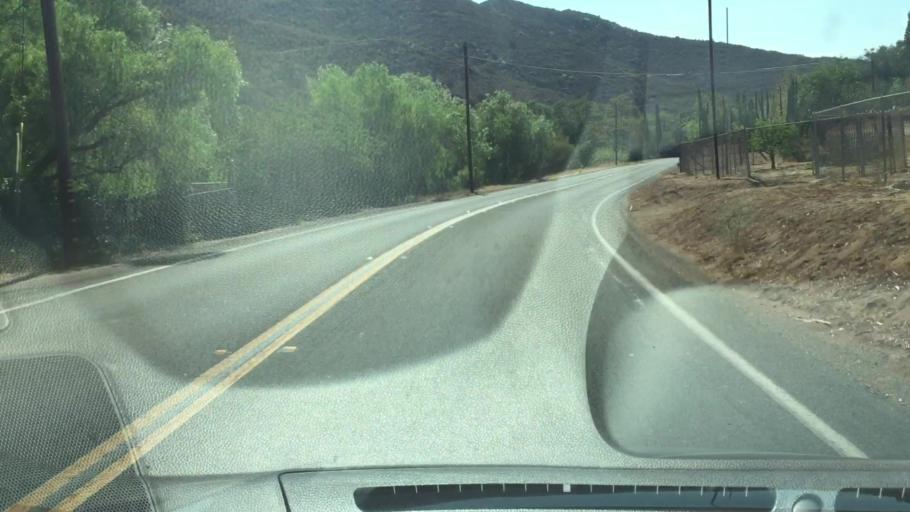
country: US
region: California
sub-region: San Diego County
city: Jamul
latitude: 32.7345
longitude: -116.8880
